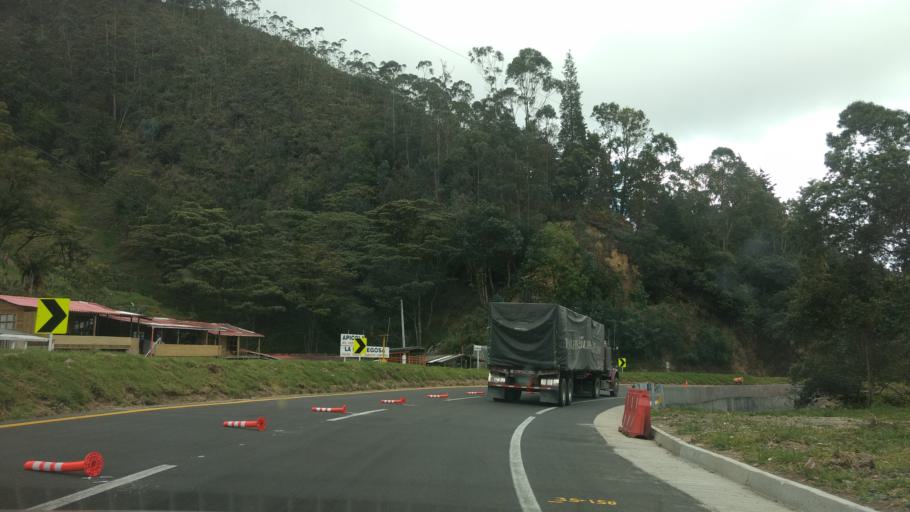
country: CO
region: Cundinamarca
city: San Francisco
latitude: 4.9248
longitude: -74.2922
